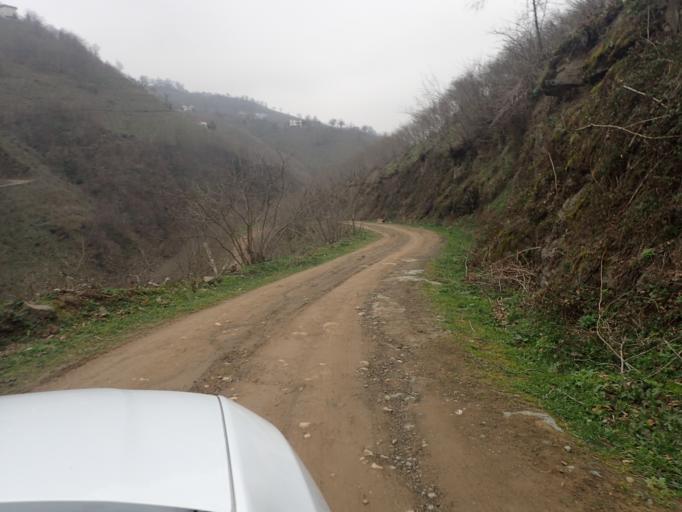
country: TR
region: Ordu
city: Camas
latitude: 40.8997
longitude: 37.5553
